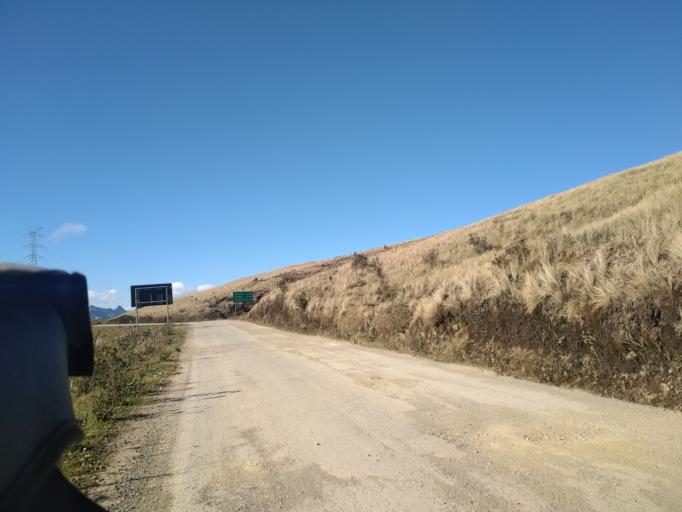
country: PE
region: Amazonas
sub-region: Provincia de Chachapoyas
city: Montevideo
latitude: -6.7312
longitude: -77.8948
